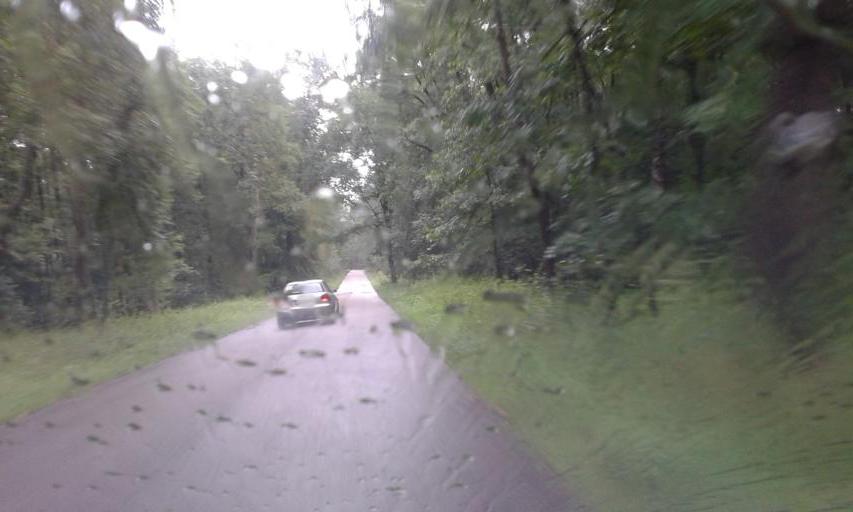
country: PL
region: West Pomeranian Voivodeship
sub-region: Powiat szczecinecki
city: Borne Sulinowo
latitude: 53.5323
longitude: 16.4946
